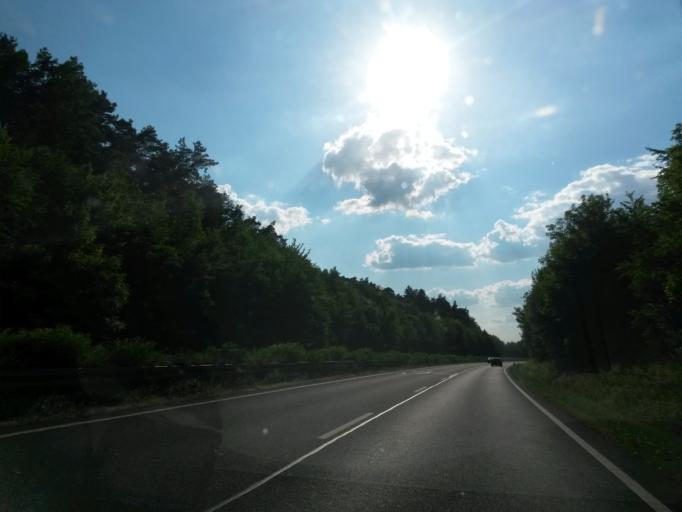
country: DE
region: Bavaria
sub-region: Regierungsbezirk Mittelfranken
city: Langenzenn
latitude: 49.4823
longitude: 10.7958
